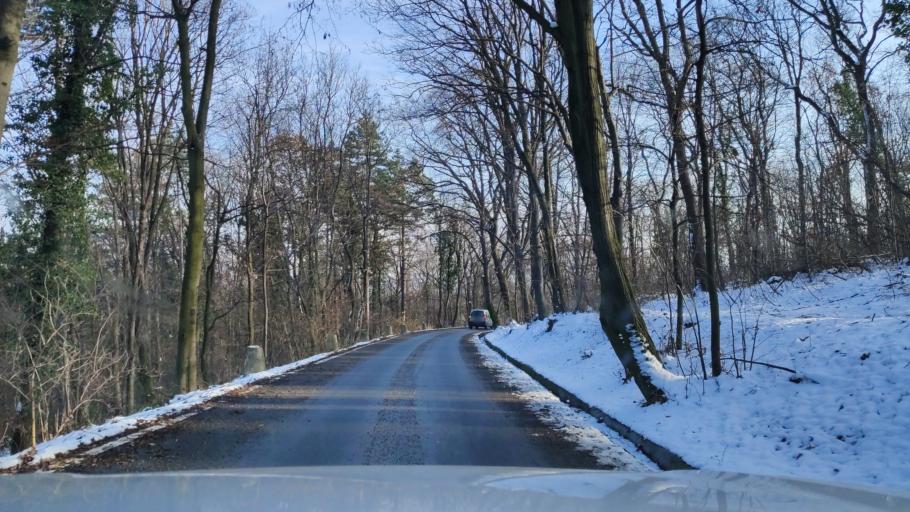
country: RS
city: Rusanj
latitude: 44.6980
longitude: 20.5196
